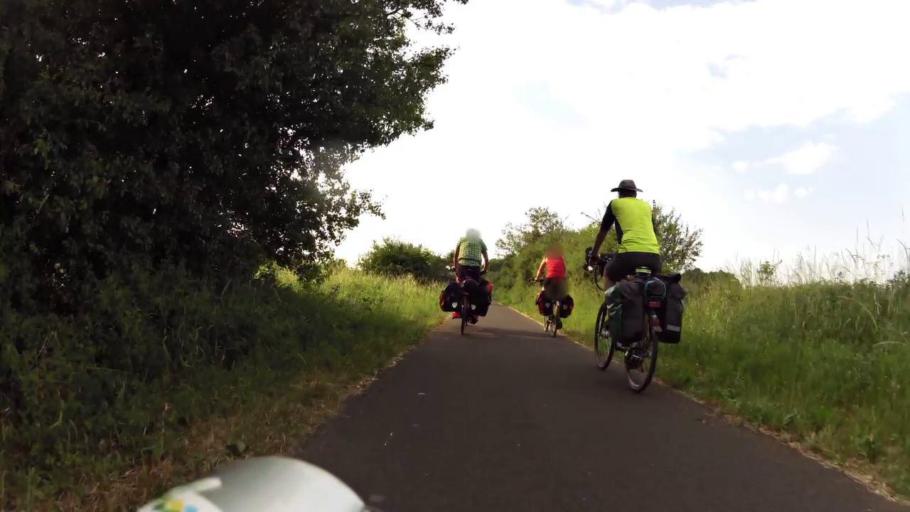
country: PL
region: Kujawsko-Pomorskie
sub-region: Powiat torunski
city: Lubianka
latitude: 53.1406
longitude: 18.4597
